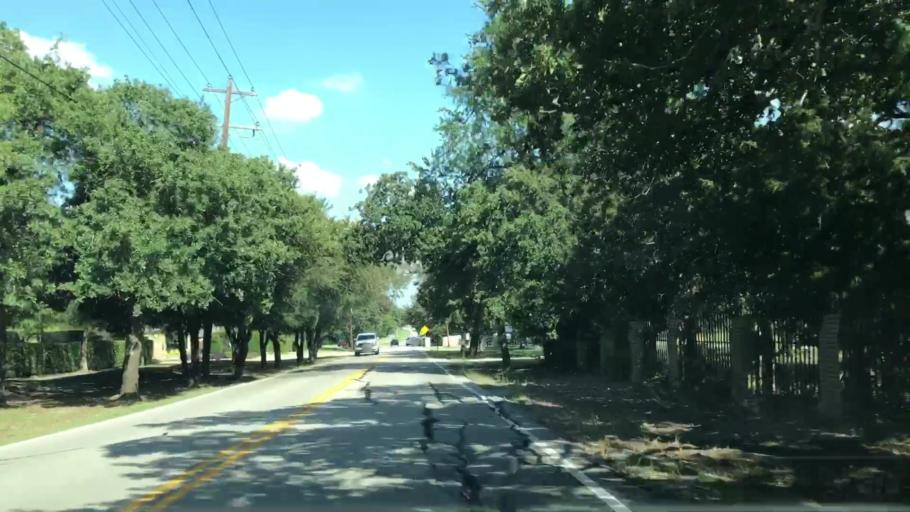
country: US
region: Texas
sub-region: Tarrant County
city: Keller
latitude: 32.9076
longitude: -97.2219
